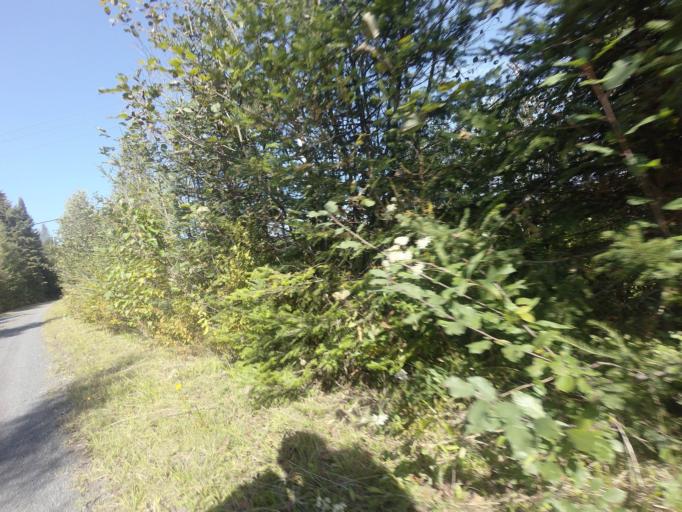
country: CA
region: Quebec
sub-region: Laurentides
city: Sainte-Agathe-des-Monts
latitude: 46.0678
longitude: -74.3131
